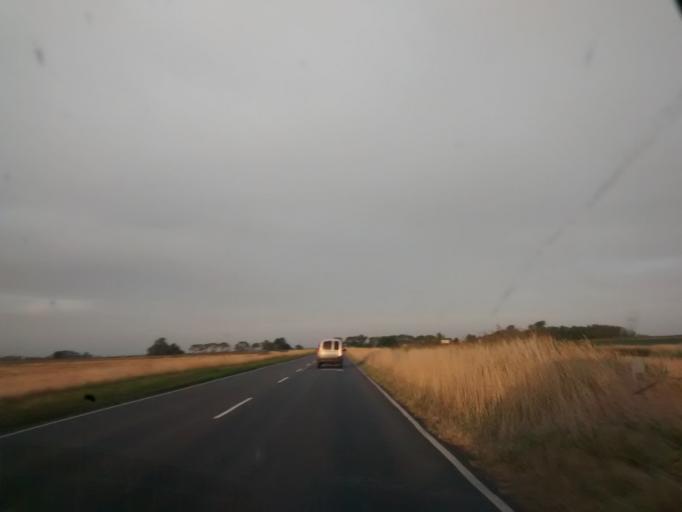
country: AR
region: Buenos Aires
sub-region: Partido de General Belgrano
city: General Belgrano
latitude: -35.8468
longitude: -58.5970
